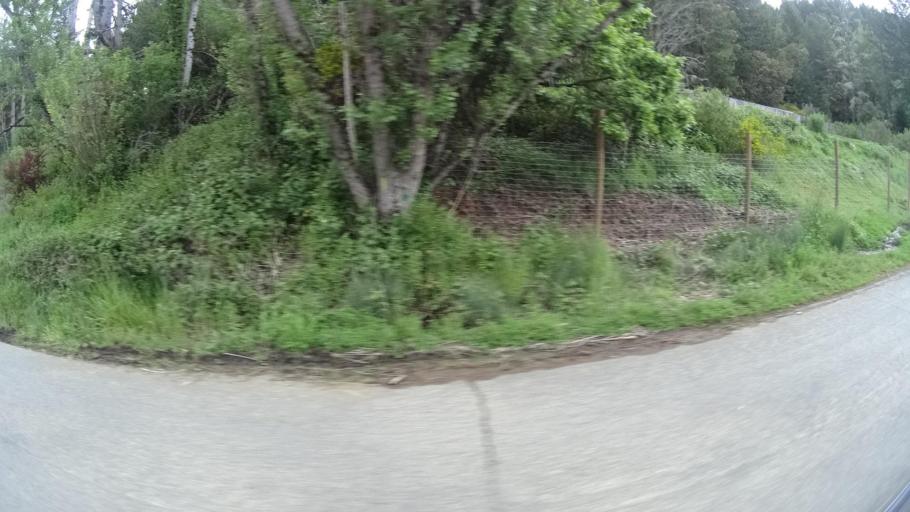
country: US
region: California
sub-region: Humboldt County
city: Redway
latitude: 40.2957
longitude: -123.8267
